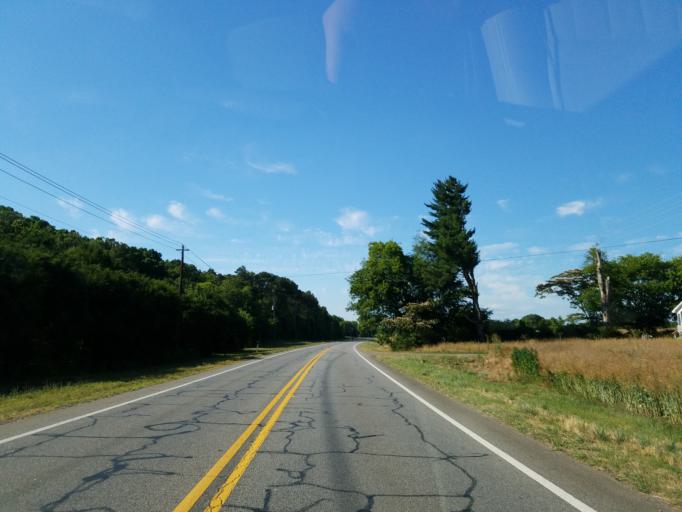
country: US
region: Georgia
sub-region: Bartow County
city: Adairsville
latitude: 34.4119
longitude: -84.9365
